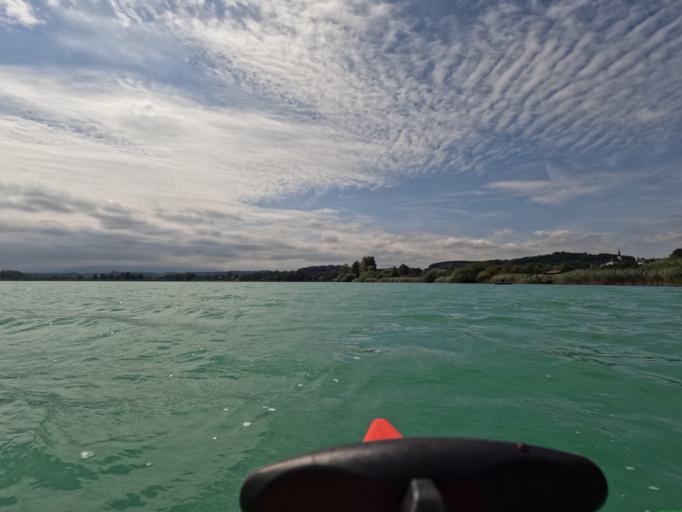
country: DE
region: Bavaria
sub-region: Upper Bavaria
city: Taching am See
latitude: 47.9661
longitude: 12.7371
